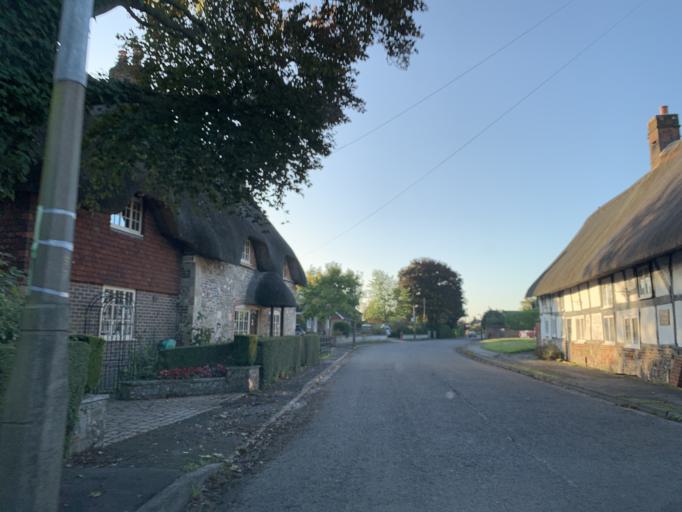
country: GB
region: England
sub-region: Wiltshire
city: Salisbury
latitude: 51.0891
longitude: -1.8112
